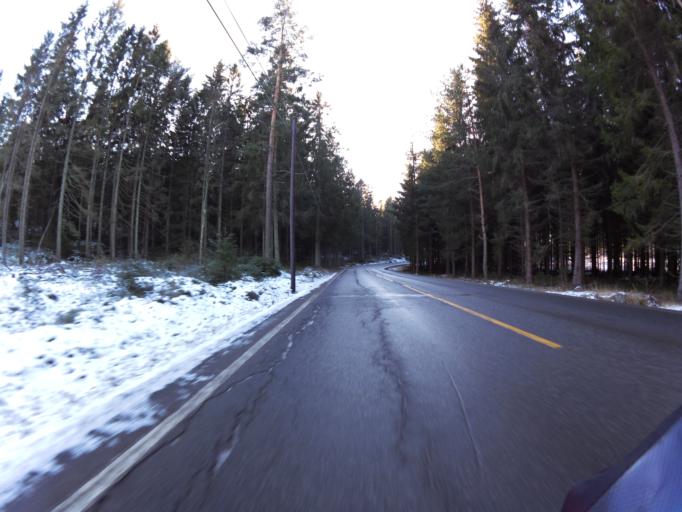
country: NO
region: Ostfold
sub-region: Fredrikstad
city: Lervik
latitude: 59.2326
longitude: 10.8178
